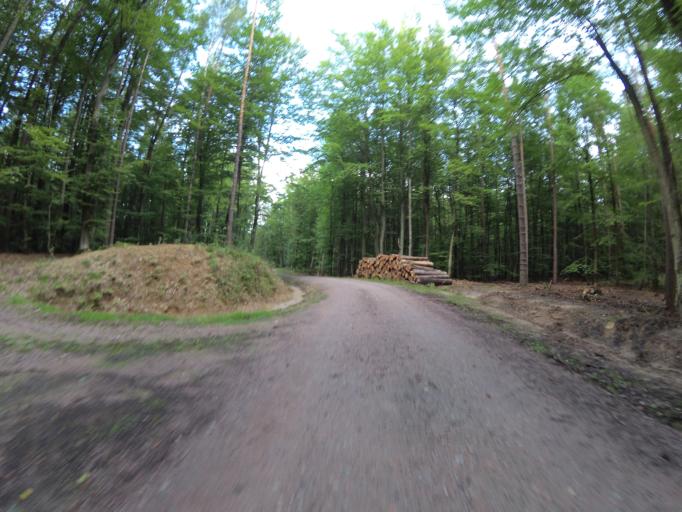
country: PL
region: Pomeranian Voivodeship
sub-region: Powiat wejherowski
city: Bojano
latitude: 54.5096
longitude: 18.4212
